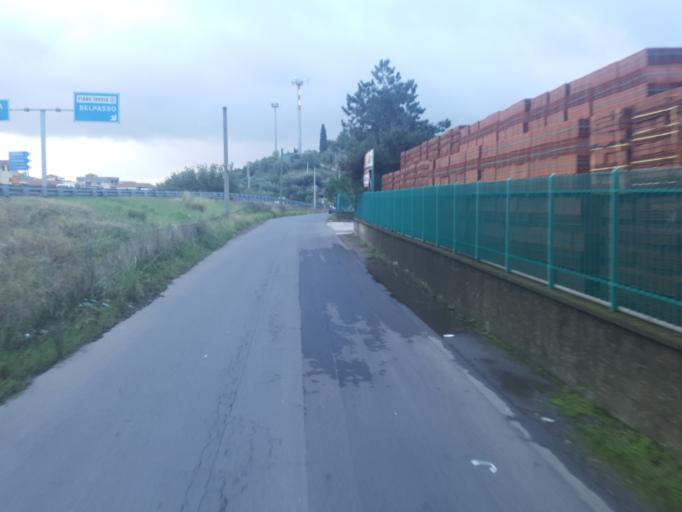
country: IT
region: Sicily
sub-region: Catania
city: Belvedere-Piano Tavola
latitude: 37.5355
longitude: 14.9819
